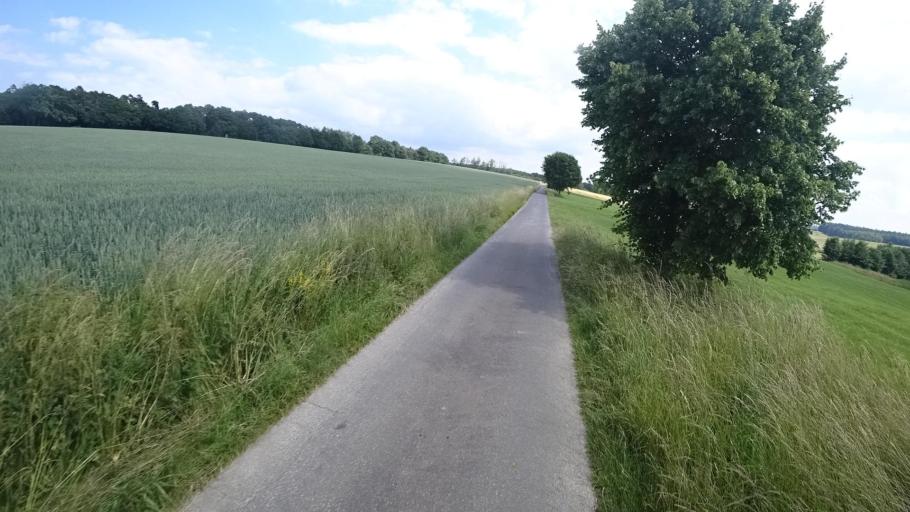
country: DE
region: Rheinland-Pfalz
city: Wolmersen
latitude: 50.7116
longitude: 7.6069
